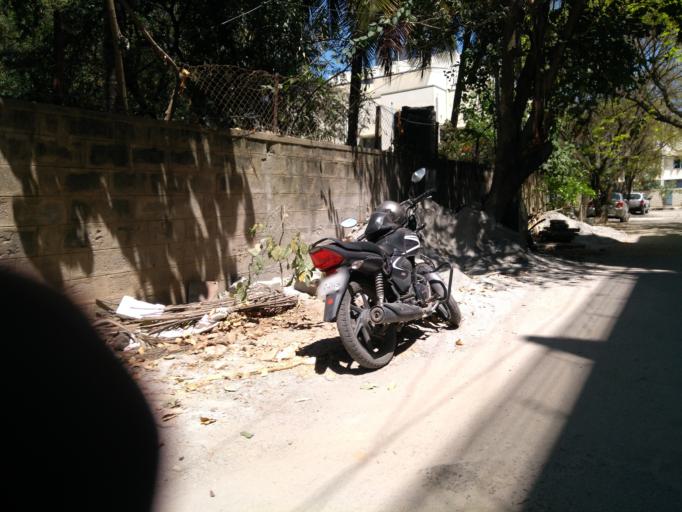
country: IN
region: Karnataka
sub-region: Bangalore Urban
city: Bangalore
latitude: 12.9683
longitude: 77.6540
